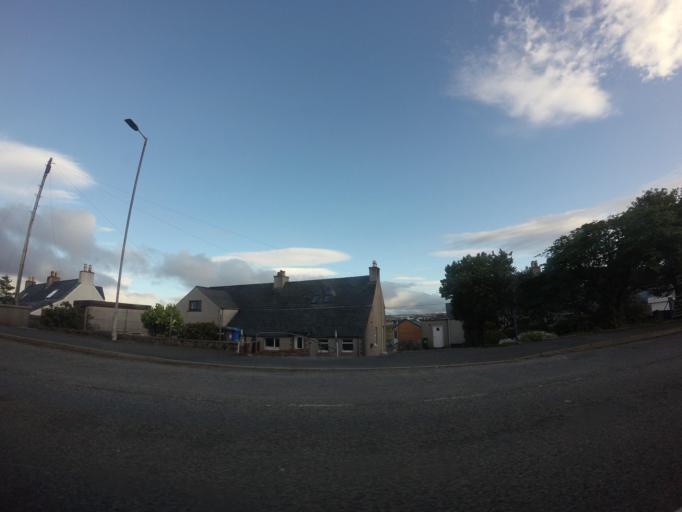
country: GB
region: Scotland
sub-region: Eilean Siar
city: Stornoway
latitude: 58.2083
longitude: -6.3659
